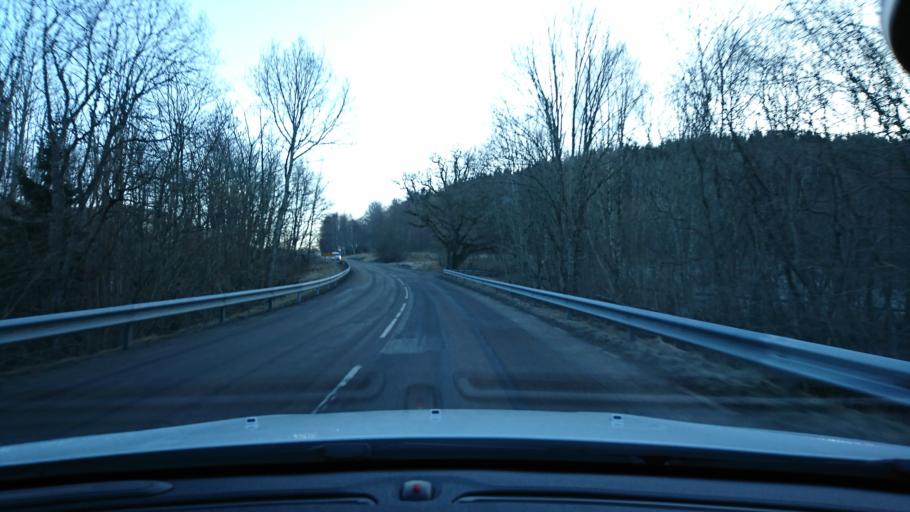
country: SE
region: Vaestra Goetaland
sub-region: Uddevalla Kommun
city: Ljungskile
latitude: 58.1996
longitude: 11.9130
